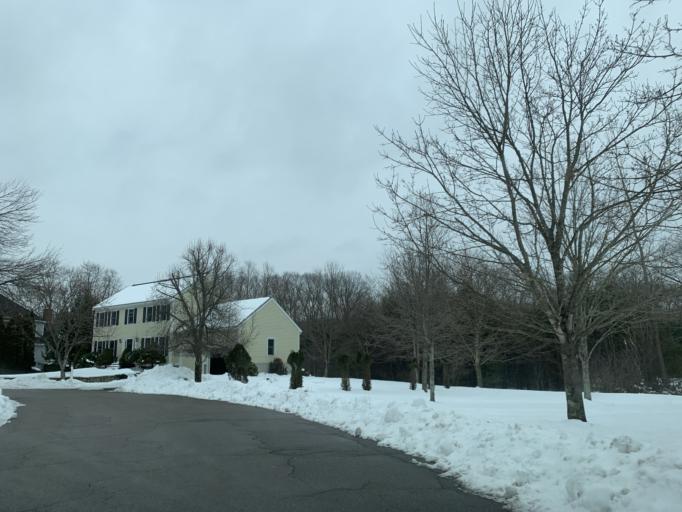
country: US
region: Massachusetts
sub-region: Norfolk County
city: Westwood
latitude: 42.2015
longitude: -71.2234
